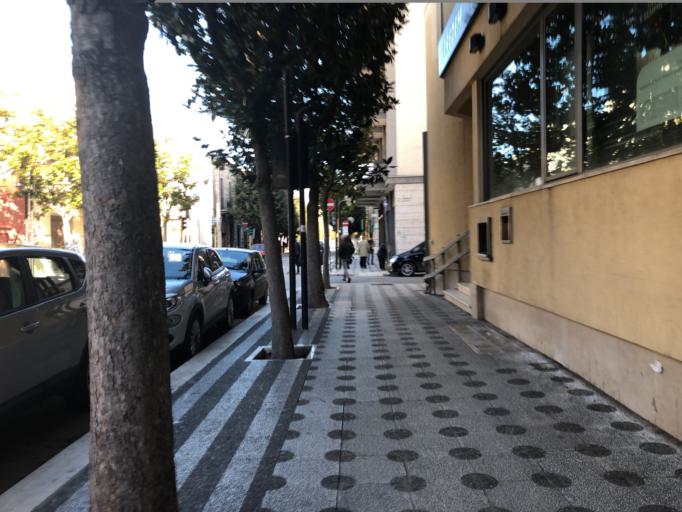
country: IT
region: Apulia
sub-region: Provincia di Barletta - Andria - Trani
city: Andria
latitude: 41.2290
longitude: 16.3014
